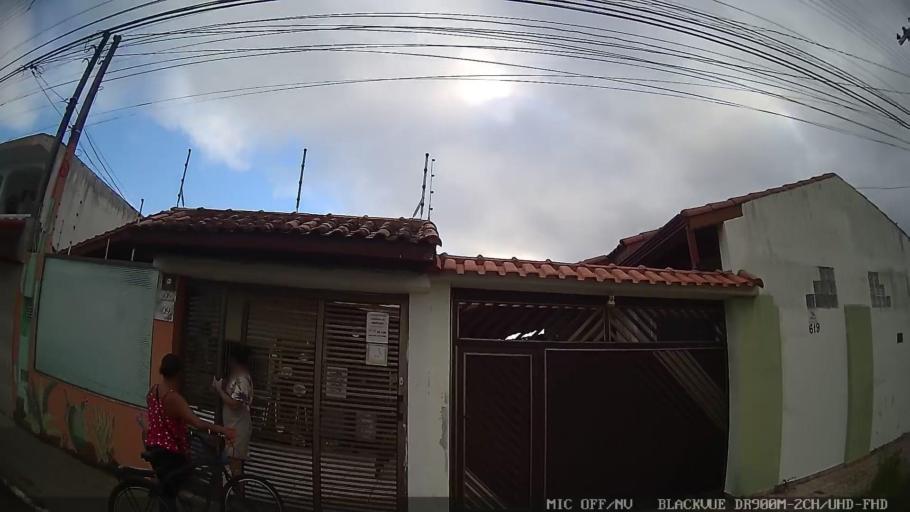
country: BR
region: Sao Paulo
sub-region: Peruibe
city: Peruibe
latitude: -24.3166
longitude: -46.9953
